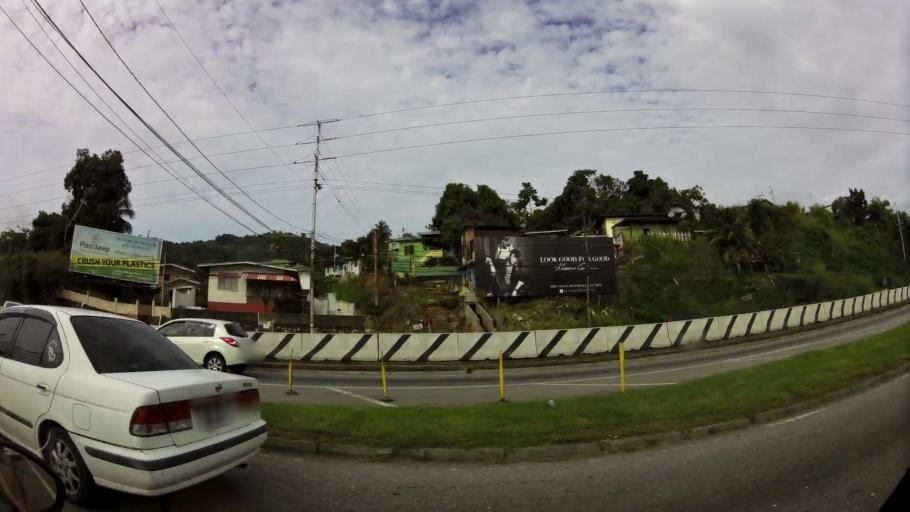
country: TT
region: City of Port of Spain
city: Mucurapo
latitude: 10.6758
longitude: -61.5444
